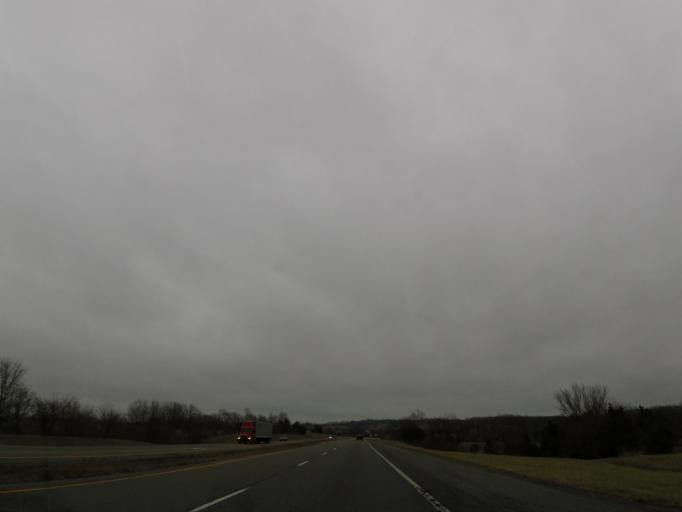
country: US
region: Kentucky
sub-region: Boyle County
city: Danville
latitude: 37.6202
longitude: -84.7408
